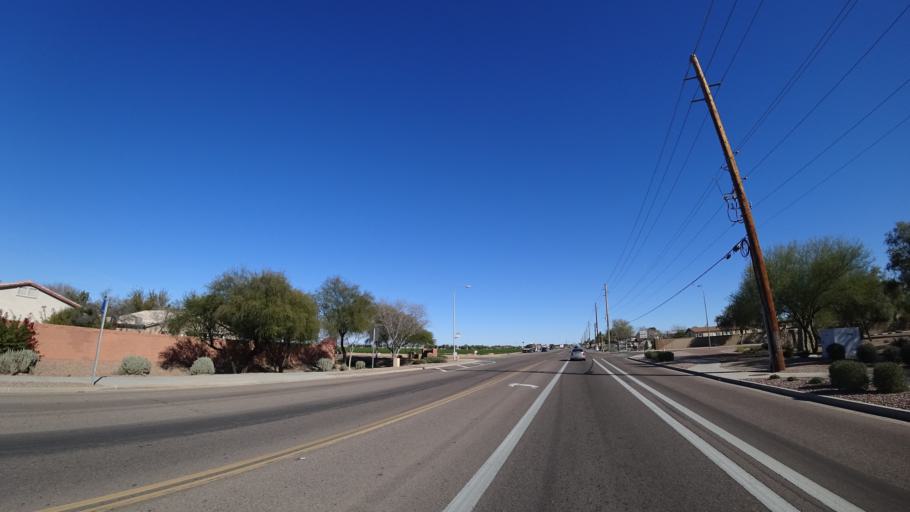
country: US
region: Arizona
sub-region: Maricopa County
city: Tolleson
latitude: 33.4229
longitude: -112.2135
